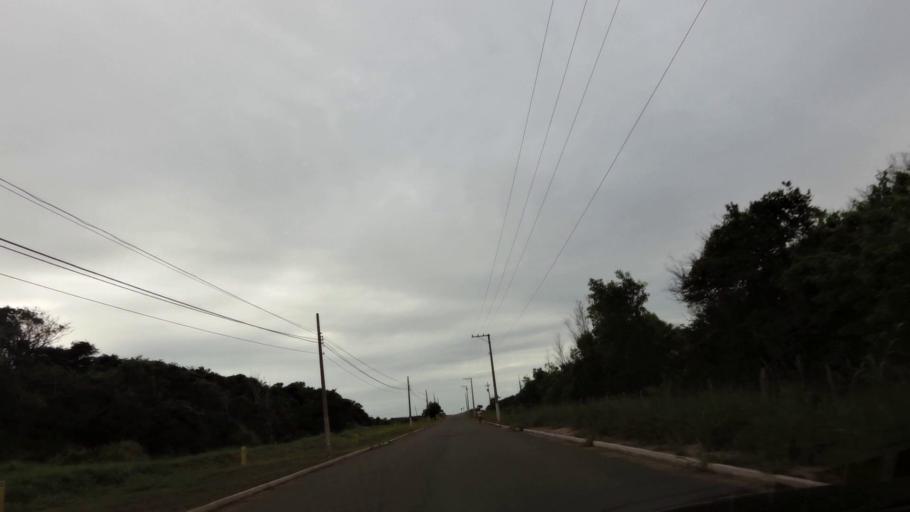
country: BR
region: Espirito Santo
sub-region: Piuma
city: Piuma
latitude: -20.8002
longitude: -40.5858
